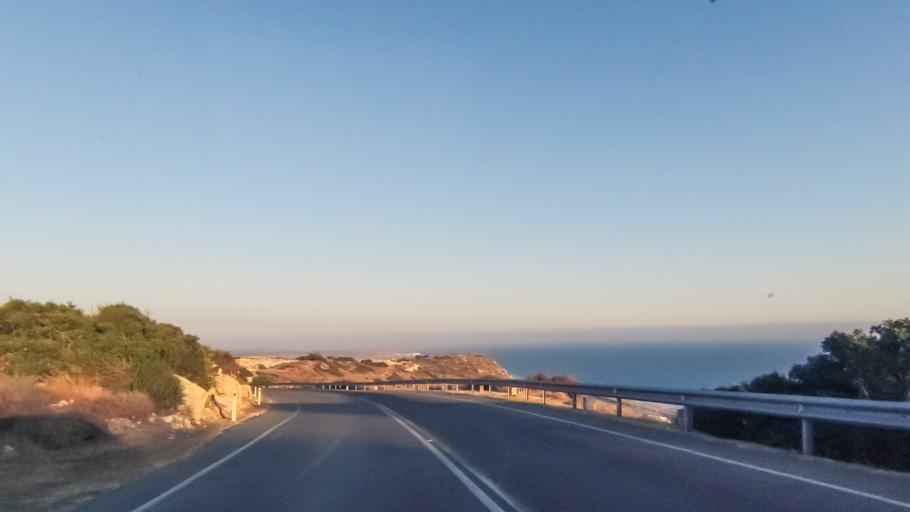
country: CY
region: Limassol
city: Erimi
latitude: 34.6695
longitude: 32.8806
